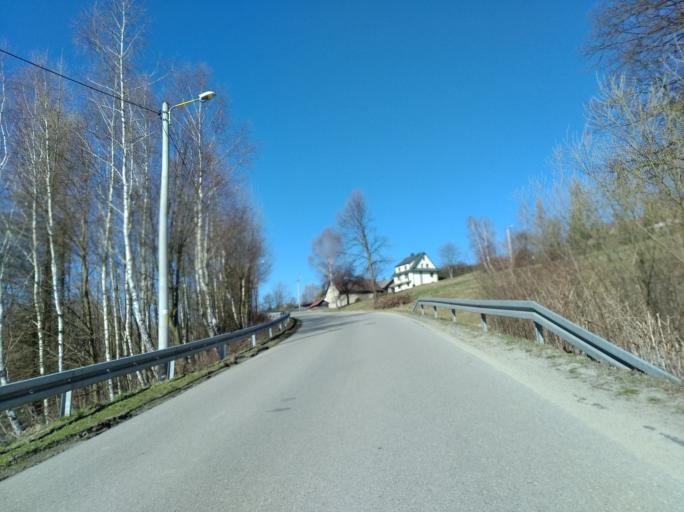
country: PL
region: Subcarpathian Voivodeship
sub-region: Powiat strzyzowski
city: Wisniowa
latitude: 49.8960
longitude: 21.6654
